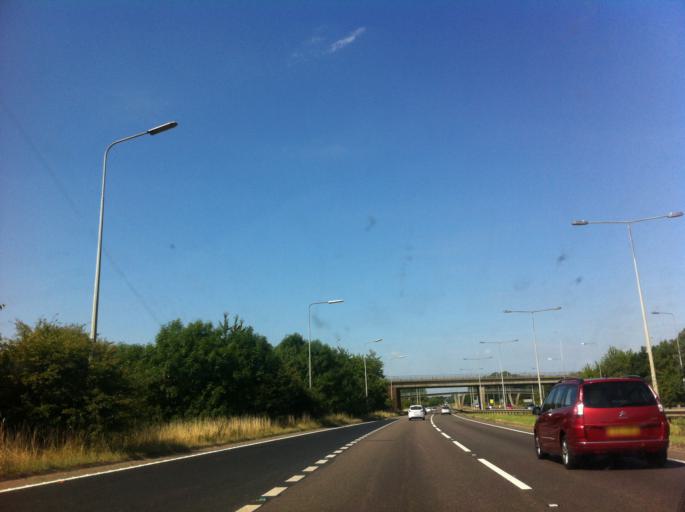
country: GB
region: England
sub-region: Northamptonshire
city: Earls Barton
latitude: 52.2543
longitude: -0.7551
